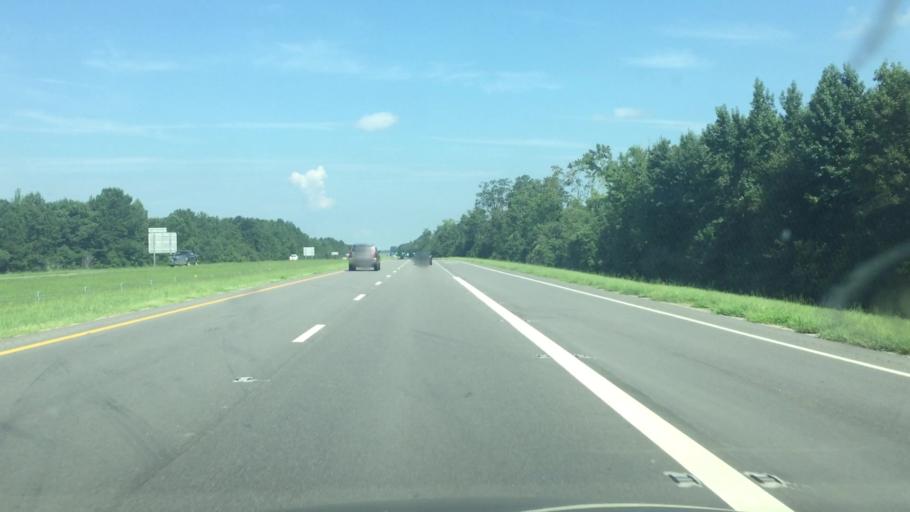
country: US
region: North Carolina
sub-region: Robeson County
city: Pembroke
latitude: 34.6548
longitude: -79.2485
